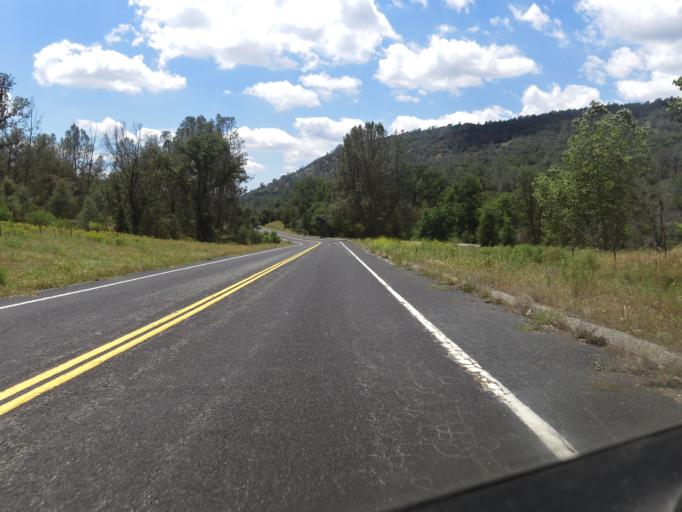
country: US
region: California
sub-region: Madera County
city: Coarsegold
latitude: 37.1893
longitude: -119.6201
